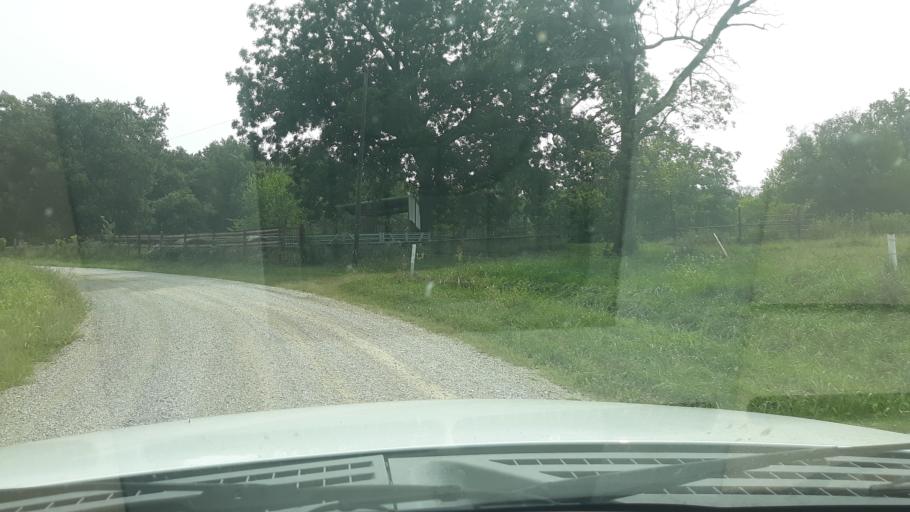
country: US
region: Illinois
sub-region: Saline County
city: Eldorado
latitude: 37.8441
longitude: -88.5166
